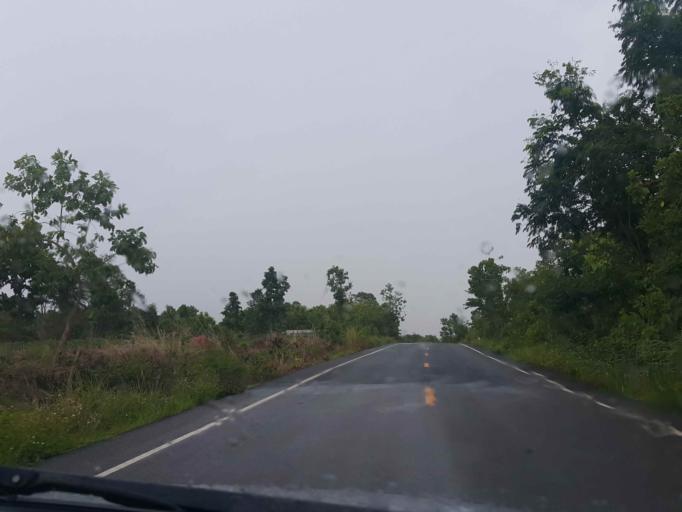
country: TH
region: Phayao
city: Dok Kham Tai
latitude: 19.0300
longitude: 99.9646
